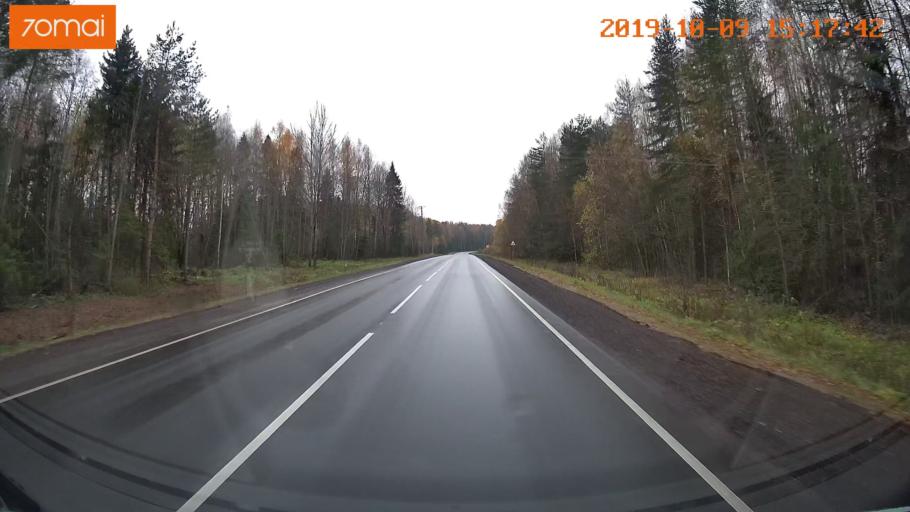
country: RU
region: Kostroma
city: Susanino
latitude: 58.0949
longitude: 41.5818
